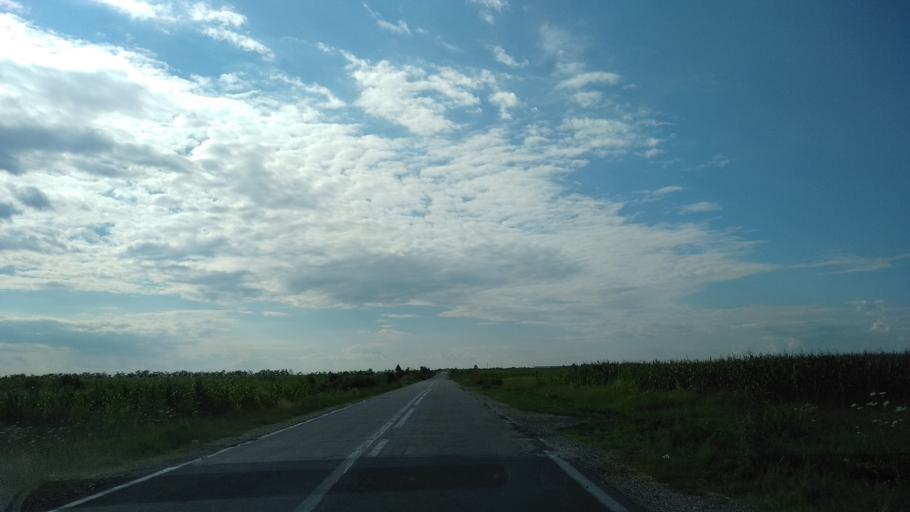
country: RO
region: Dambovita
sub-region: Comuna Mogosani
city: Zavoiu
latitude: 44.6215
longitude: 25.3768
